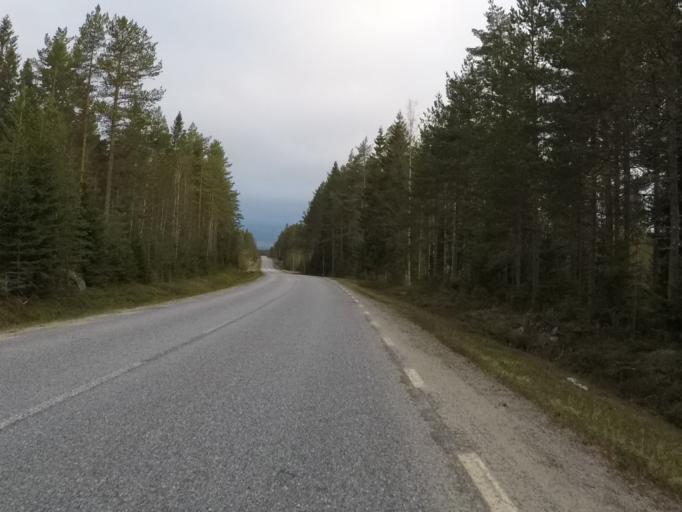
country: SE
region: Vaesterbotten
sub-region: Robertsfors Kommun
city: Robertsfors
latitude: 63.9529
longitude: 20.7942
